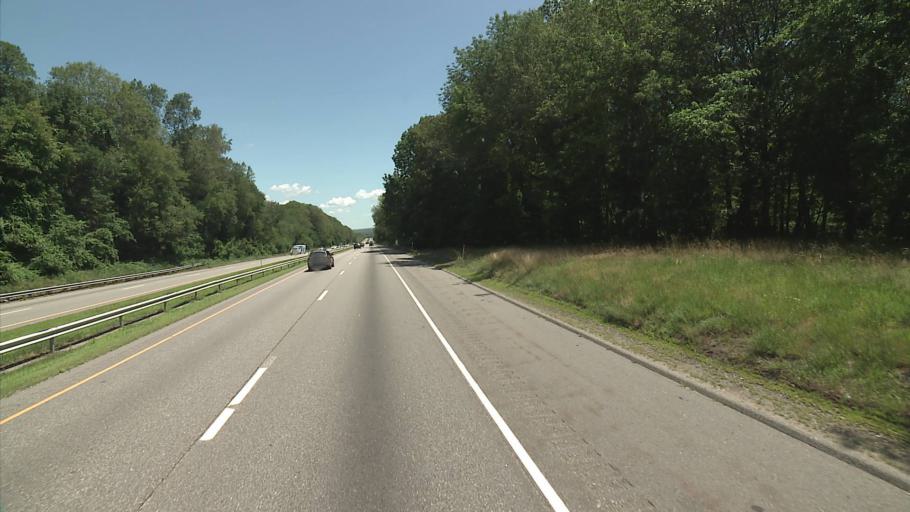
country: US
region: Connecticut
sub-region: New London County
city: Baltic
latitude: 41.5728
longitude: -72.0860
